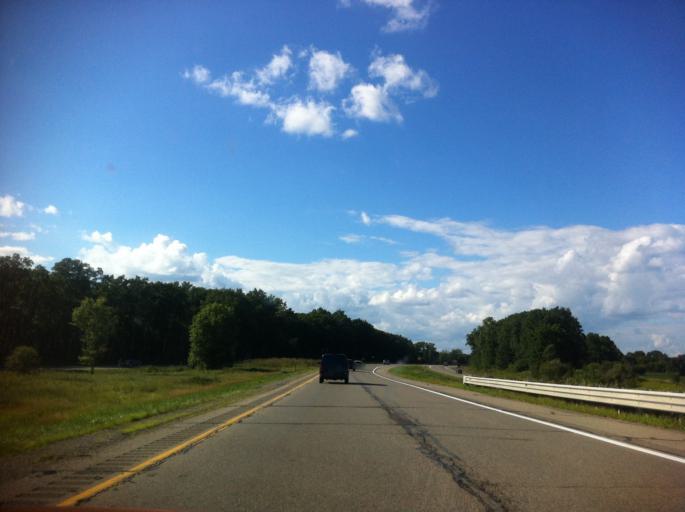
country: US
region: Michigan
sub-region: Washtenaw County
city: Ann Arbor
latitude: 42.3211
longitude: -83.7398
